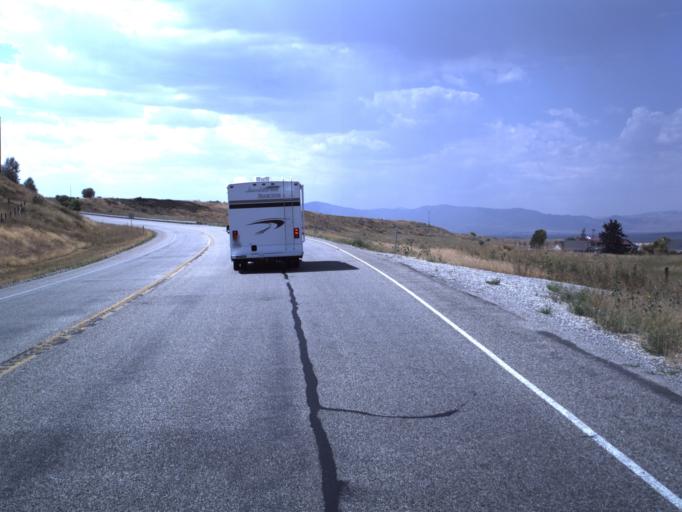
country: US
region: Utah
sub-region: Cache County
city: Mendon
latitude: 41.7962
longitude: -112.0434
